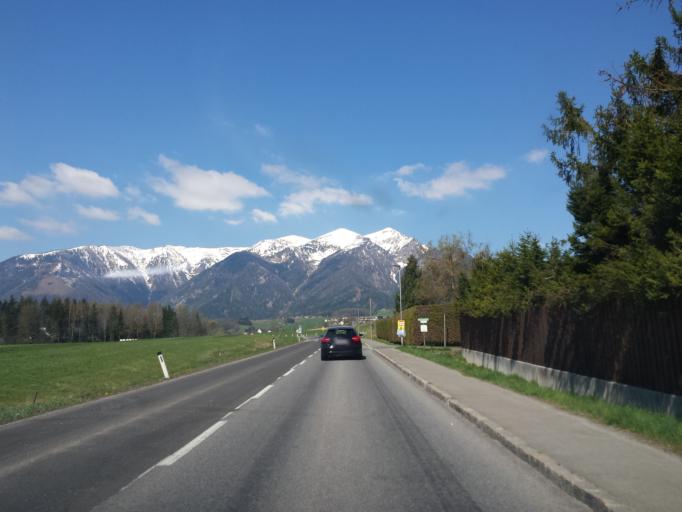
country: AT
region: Styria
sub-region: Politischer Bezirk Leoben
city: Trofaiach
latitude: 47.4059
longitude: 14.9889
